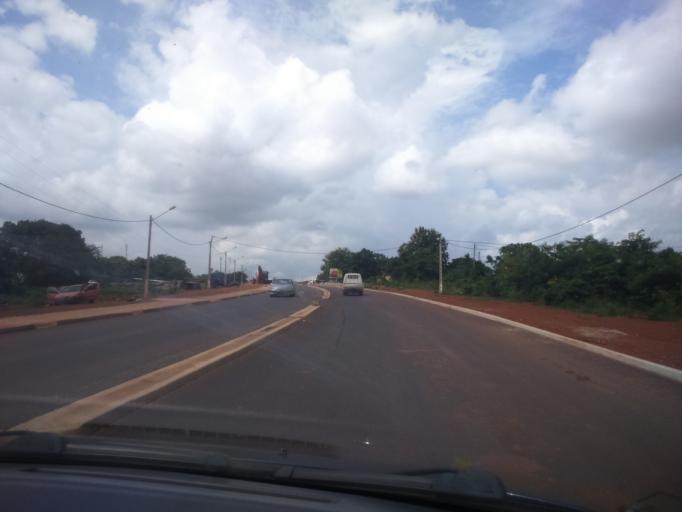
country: CI
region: Moyen-Comoe
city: Abengourou
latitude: 6.7184
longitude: -3.5183
